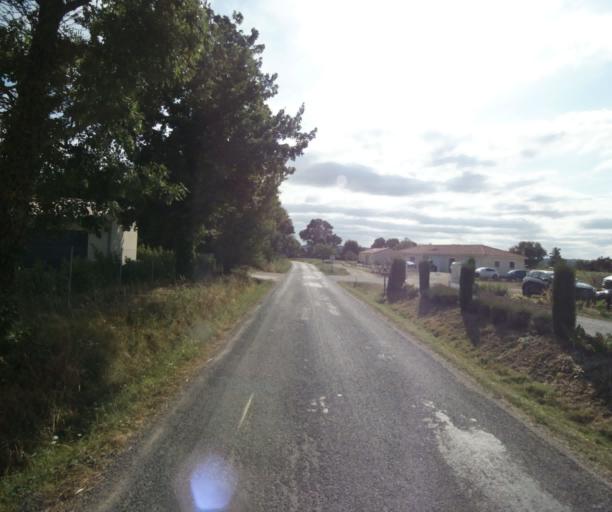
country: FR
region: Midi-Pyrenees
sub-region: Departement du Tarn
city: Puylaurens
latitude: 43.5321
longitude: 1.9856
